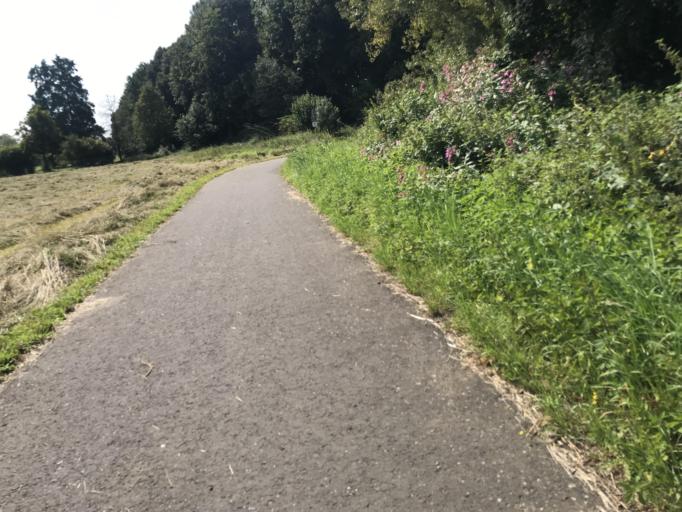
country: DE
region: Hesse
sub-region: Regierungsbezirk Giessen
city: Hungen
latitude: 50.4624
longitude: 8.9170
